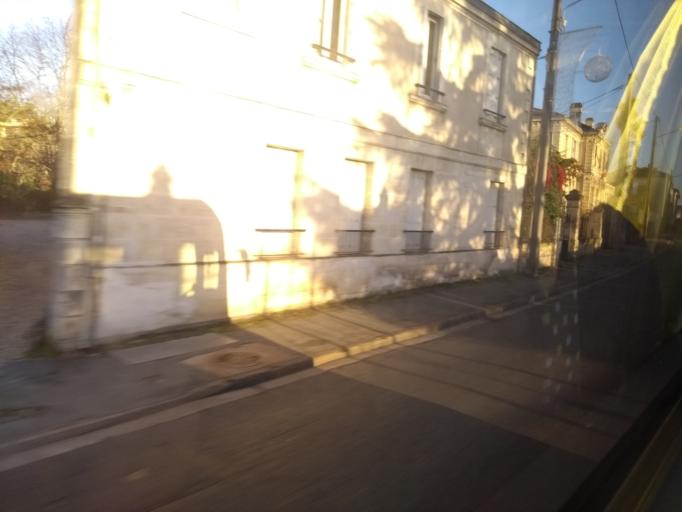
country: FR
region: Aquitaine
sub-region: Departement de la Gironde
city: Gradignan
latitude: 44.7706
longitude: -0.6156
